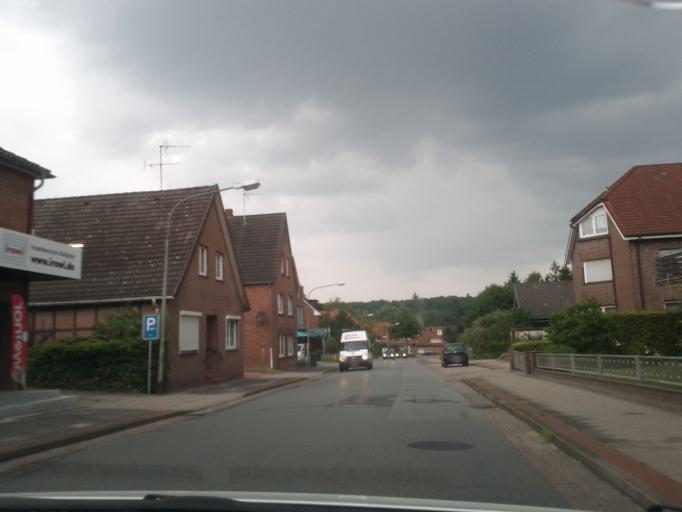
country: DE
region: Lower Saxony
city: Harsefeld
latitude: 53.4551
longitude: 9.4995
